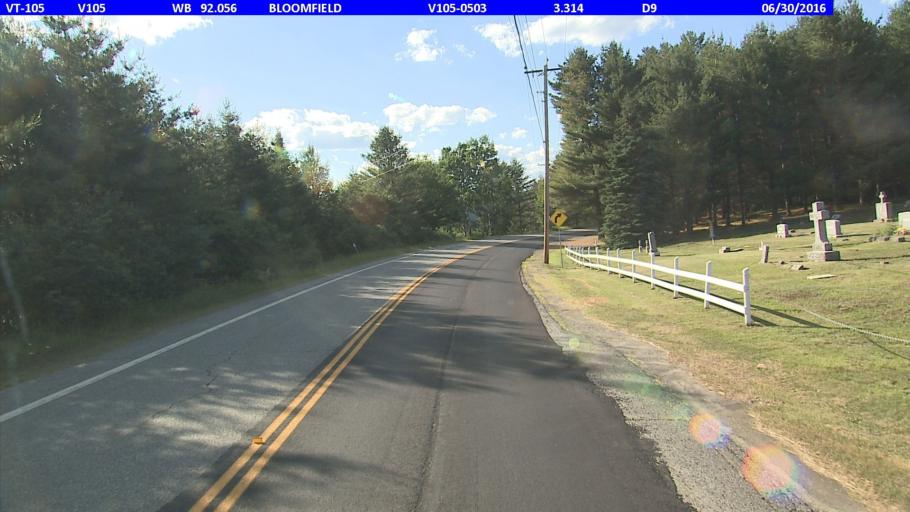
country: US
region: New Hampshire
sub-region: Coos County
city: Stratford
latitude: 44.7622
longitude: -71.6452
